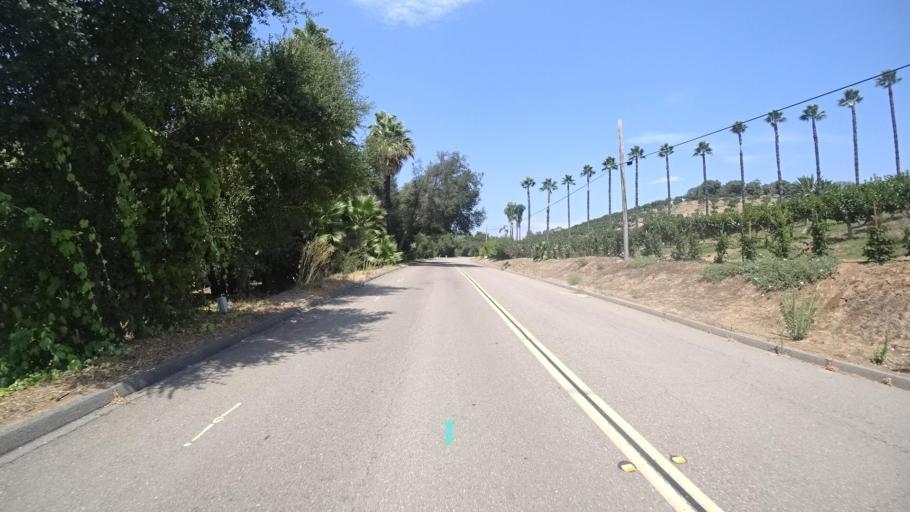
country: US
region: California
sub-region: San Diego County
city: Bonsall
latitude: 33.3049
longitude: -117.2159
